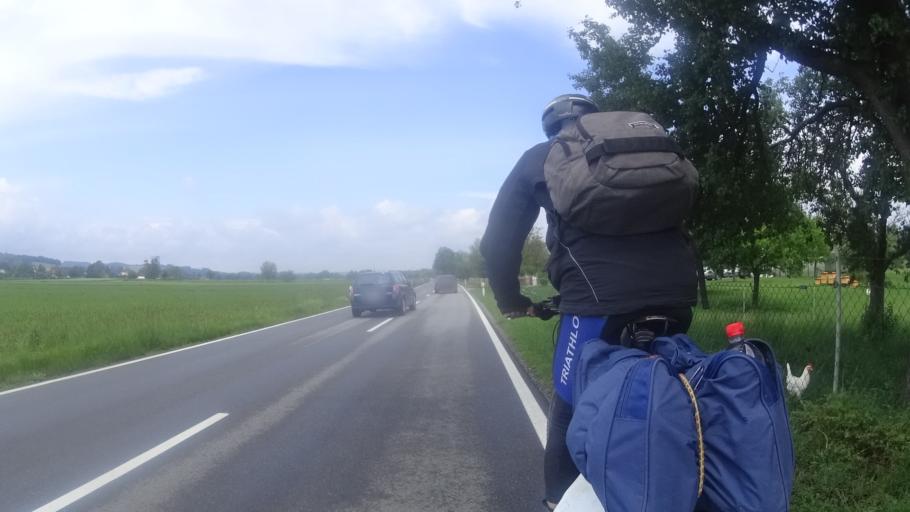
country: DE
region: Bavaria
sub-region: Lower Bavaria
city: Bayerbach
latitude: 48.4261
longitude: 13.1207
